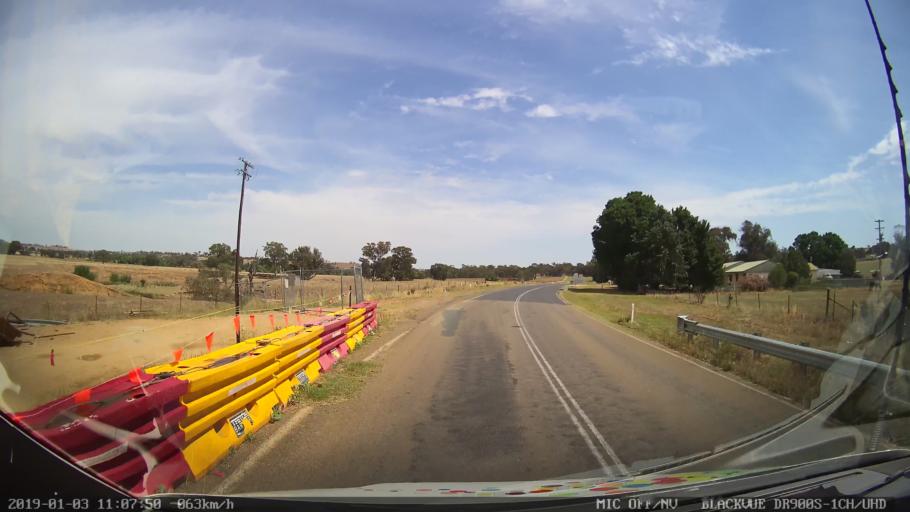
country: AU
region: New South Wales
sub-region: Young
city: Young
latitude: -34.2556
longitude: 148.2592
